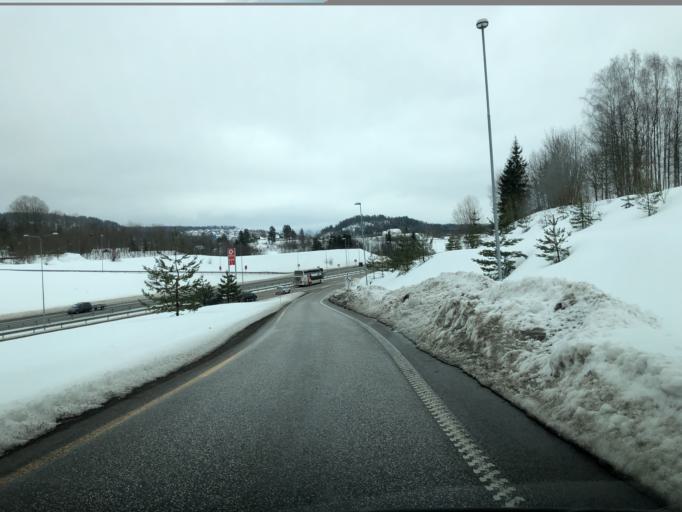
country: NO
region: Vestfold
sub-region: Holmestrand
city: Gullhaug
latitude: 59.5134
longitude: 10.2030
